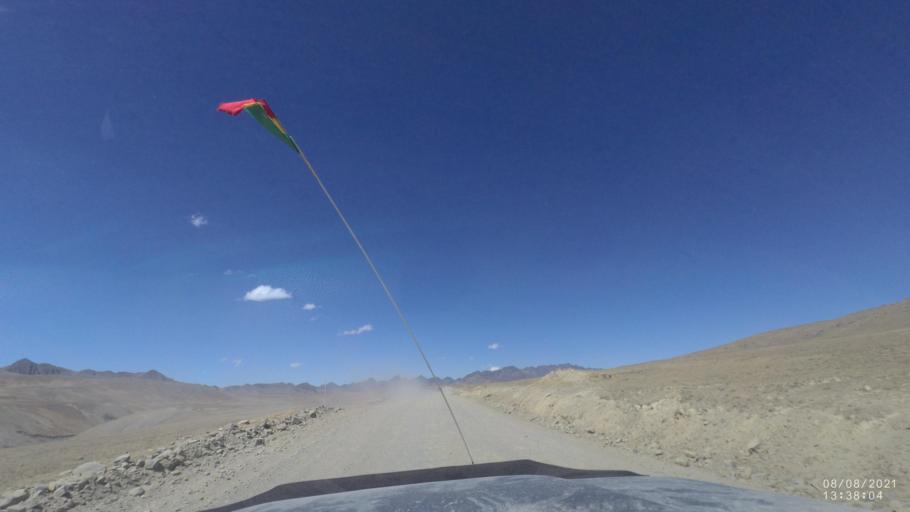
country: BO
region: Cochabamba
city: Colchani
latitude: -17.0839
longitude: -66.4908
